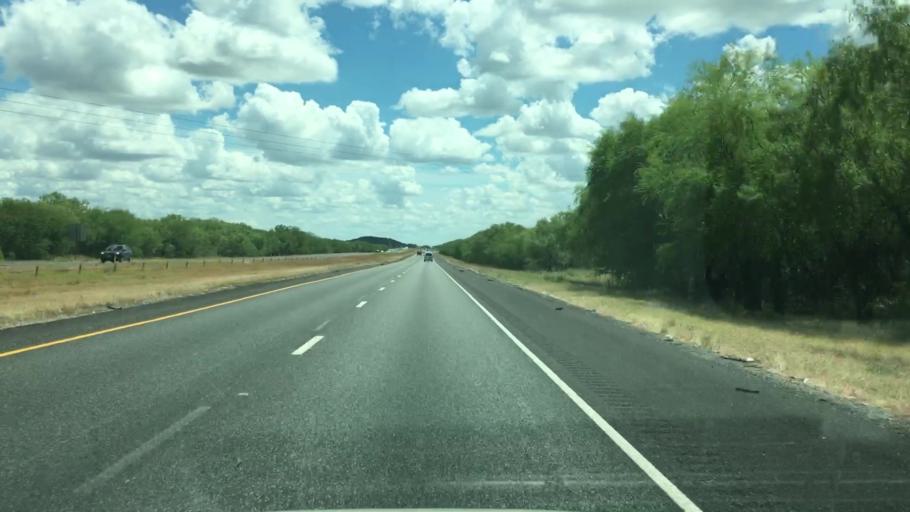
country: US
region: Texas
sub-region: Atascosa County
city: Pleasanton
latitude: 28.7457
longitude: -98.2936
